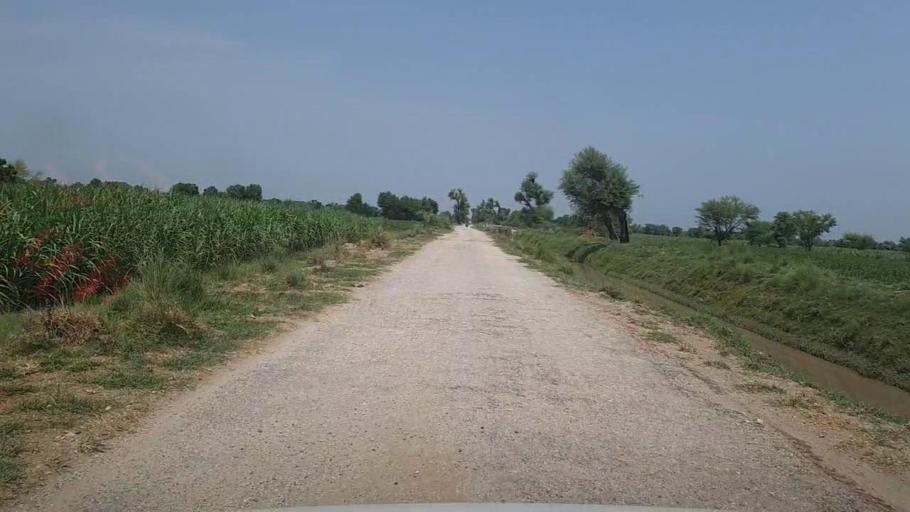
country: PK
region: Sindh
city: Karaundi
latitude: 26.8883
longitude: 68.3336
